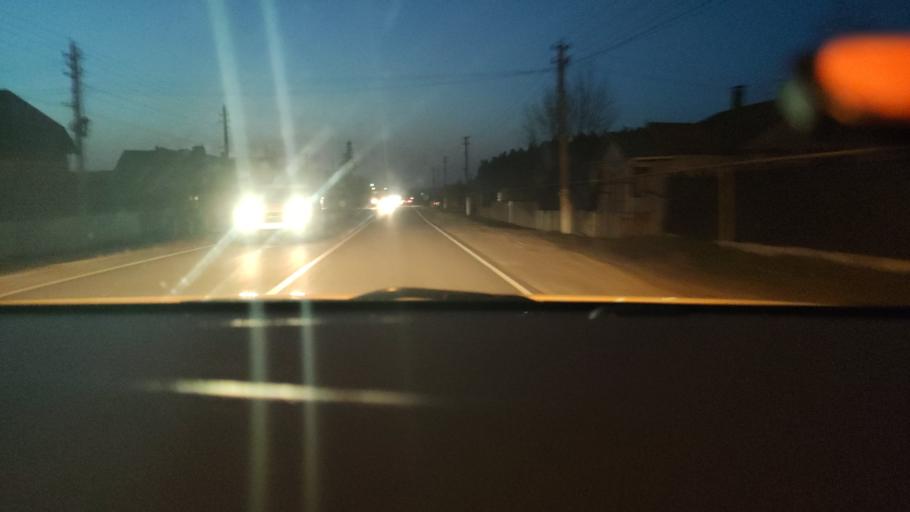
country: RU
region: Voronezj
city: Shilovo
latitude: 51.5835
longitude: 39.0346
